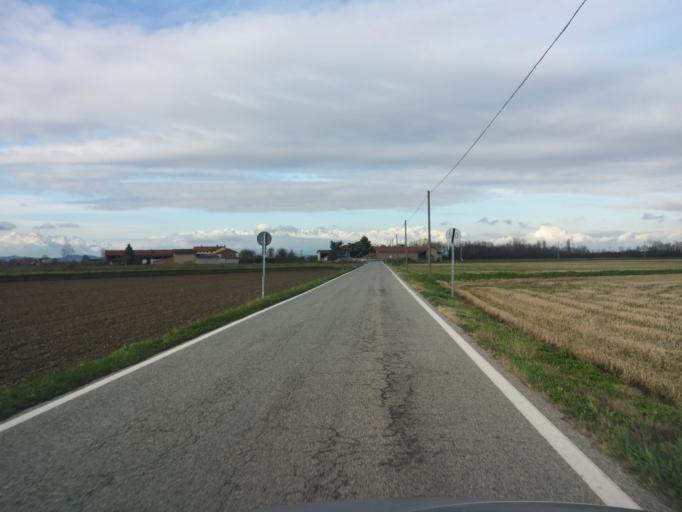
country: IT
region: Piedmont
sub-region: Provincia di Vercelli
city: Crova
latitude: 45.3232
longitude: 8.1937
